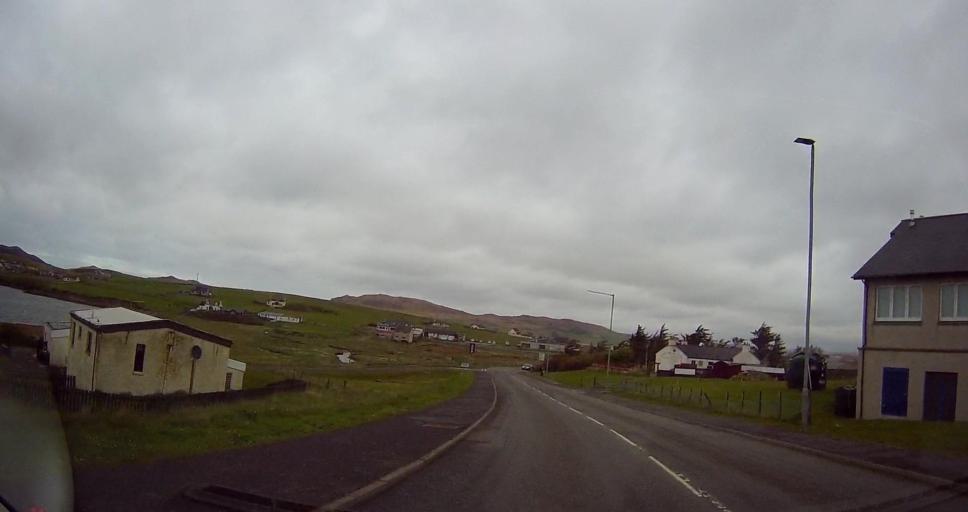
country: GB
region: Scotland
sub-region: Shetland Islands
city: Lerwick
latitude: 60.3936
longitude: -1.3507
